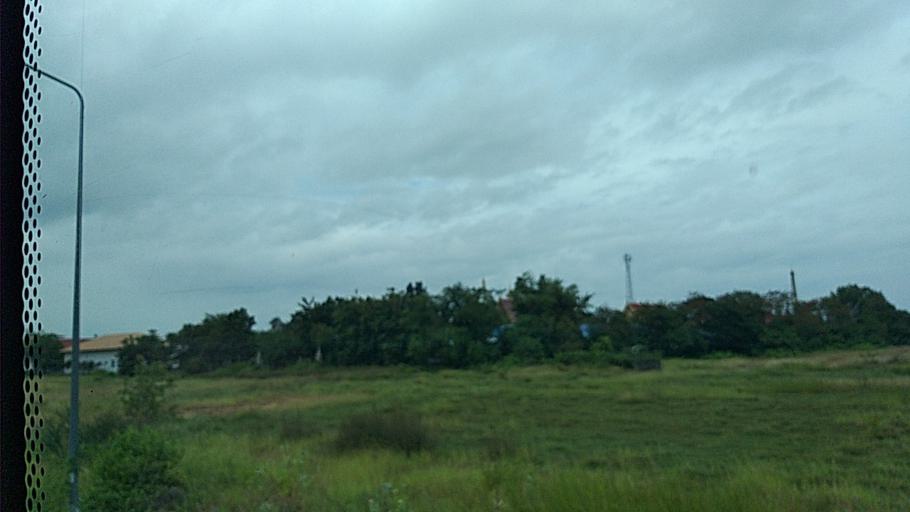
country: TH
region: Maha Sarakham
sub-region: Amphoe Borabue
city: Borabue
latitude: 16.0385
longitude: 103.1262
